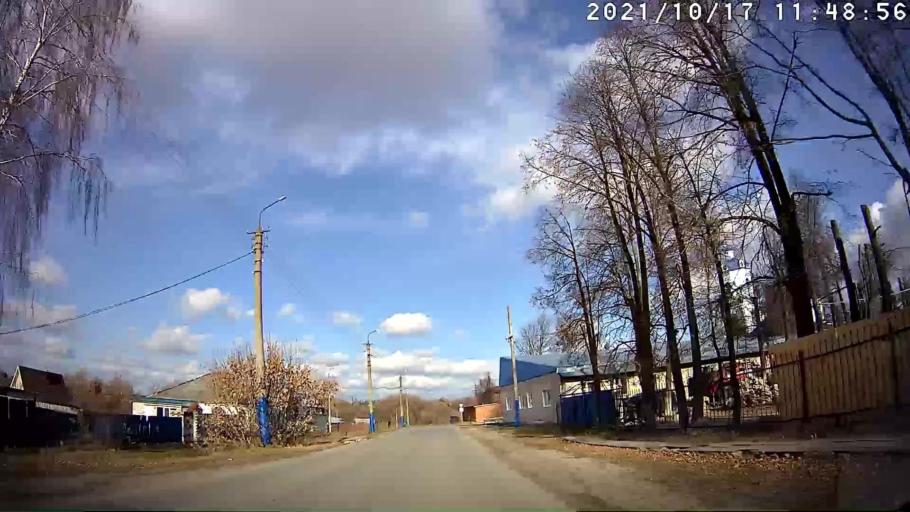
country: RU
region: Mariy-El
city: Kuzhener
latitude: 57.0049
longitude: 48.7347
